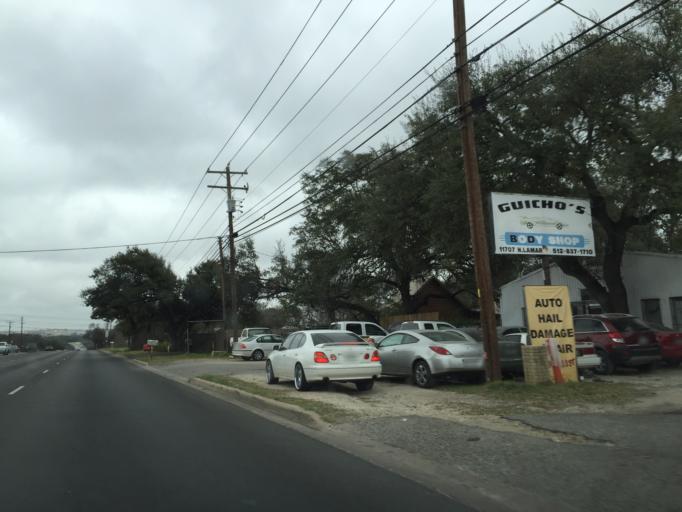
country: US
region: Texas
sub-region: Travis County
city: Wells Branch
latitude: 30.3869
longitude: -97.6839
